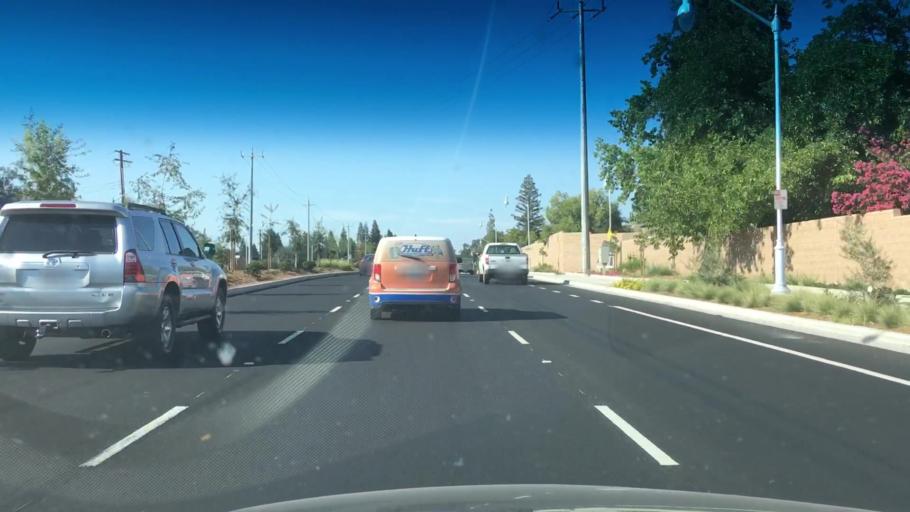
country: US
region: California
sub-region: Sacramento County
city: Orangevale
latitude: 38.6499
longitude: -121.2255
